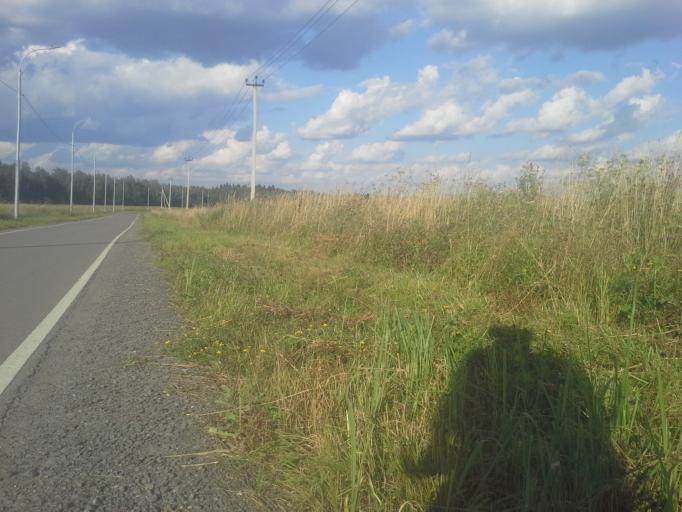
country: RU
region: Moskovskaya
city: Selyatino
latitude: 55.4295
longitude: 37.0246
